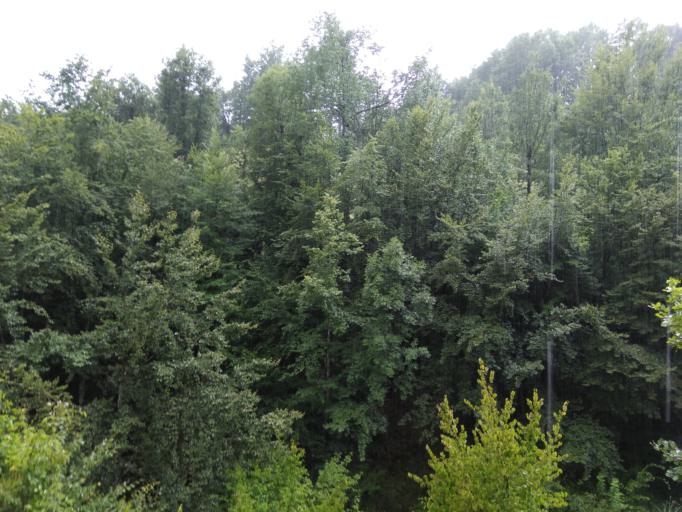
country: BG
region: Smolyan
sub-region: Obshtina Madan
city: Madan
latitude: 41.4883
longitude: 24.9160
